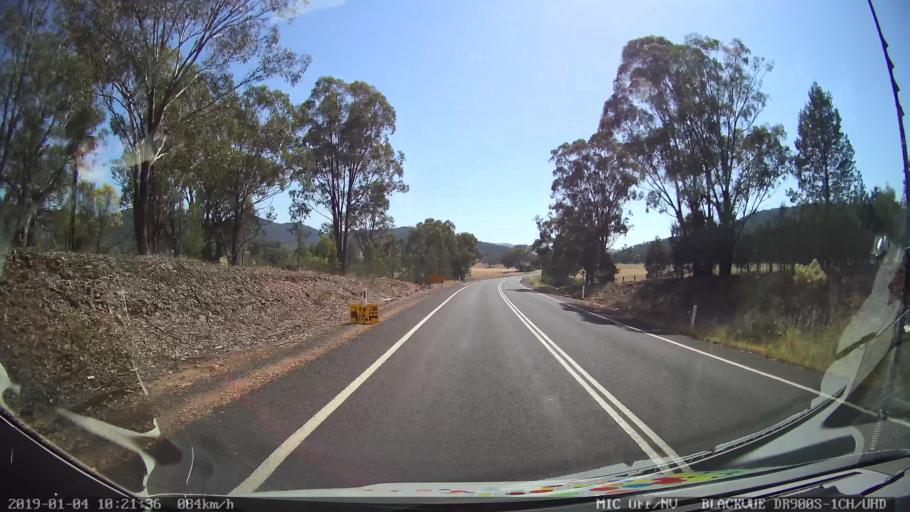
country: AU
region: New South Wales
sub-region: Cabonne
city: Canowindra
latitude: -33.3719
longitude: 148.5125
